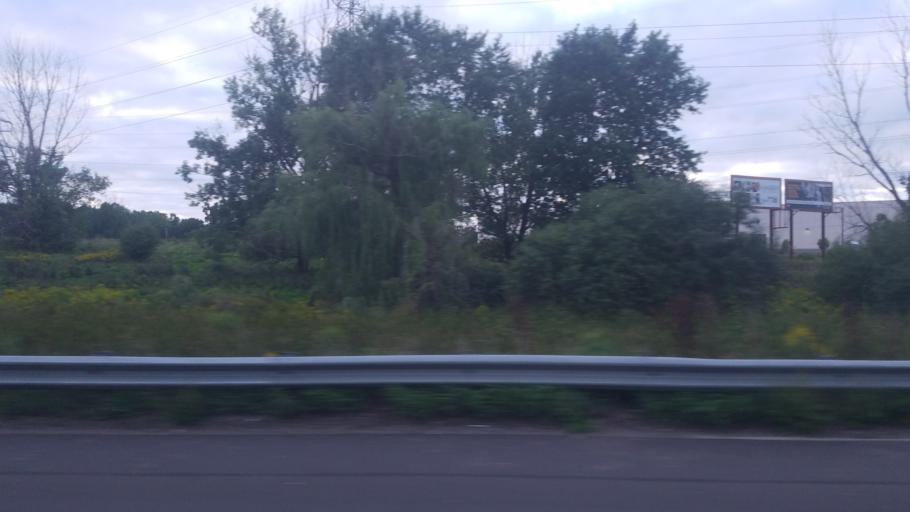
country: US
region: Minnesota
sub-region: Ramsey County
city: Lauderdale
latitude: 45.0083
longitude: -93.2047
